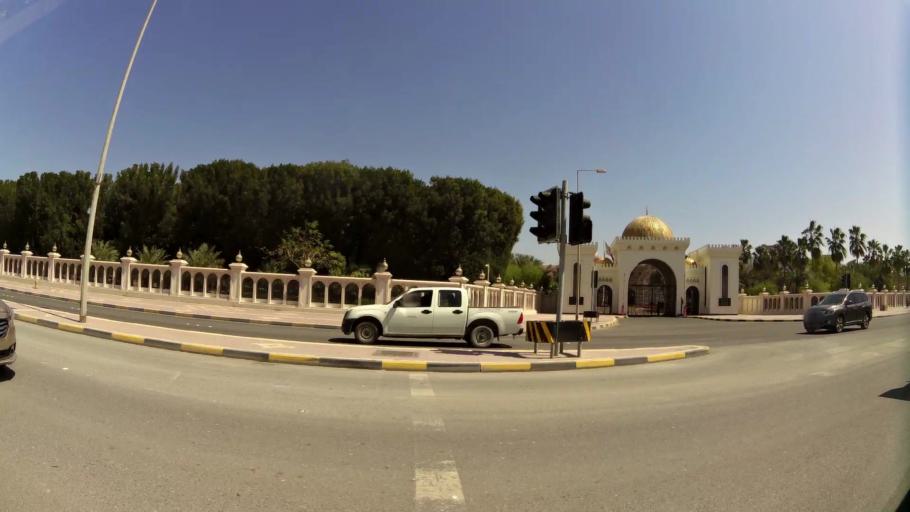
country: BH
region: Manama
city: Manama
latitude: 26.2189
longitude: 50.5900
